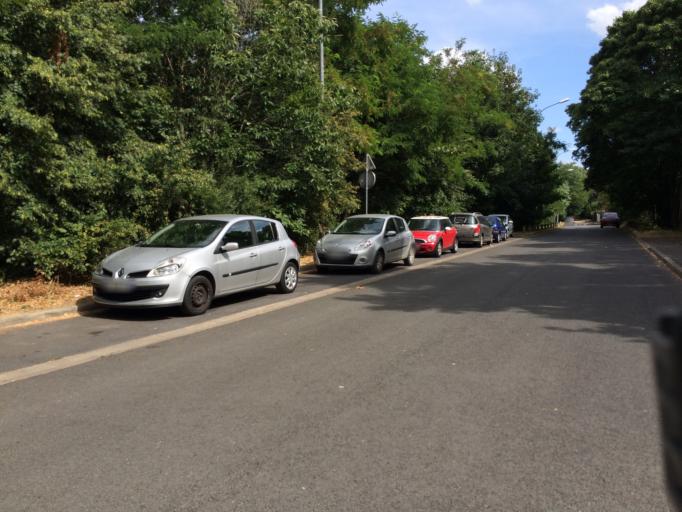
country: FR
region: Ile-de-France
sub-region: Departement de l'Essonne
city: Draveil
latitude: 48.6817
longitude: 2.4340
